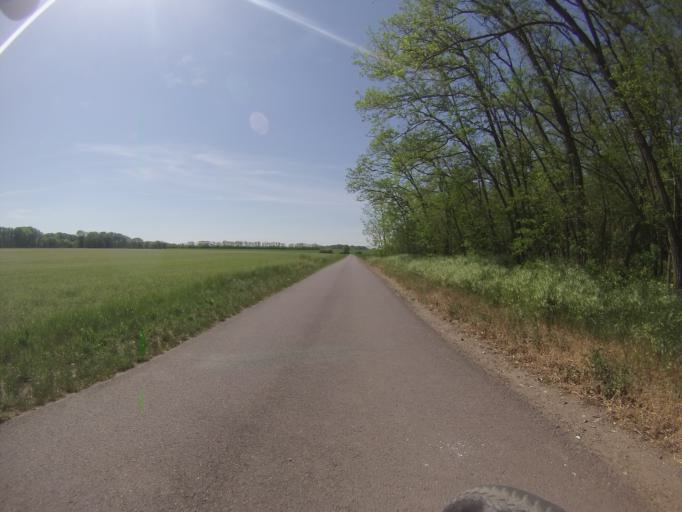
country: CZ
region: South Moravian
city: Novosedly
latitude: 48.8037
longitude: 16.4913
